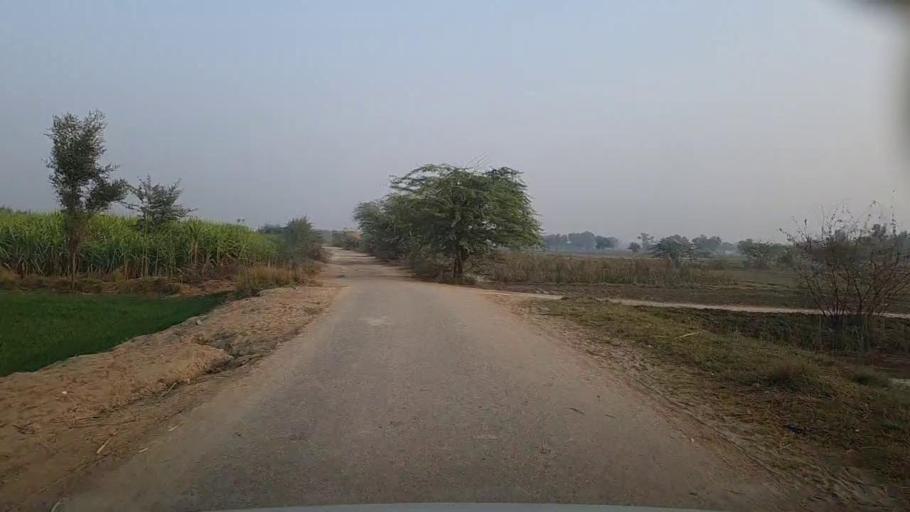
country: PK
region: Sindh
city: Bozdar
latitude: 27.0757
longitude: 68.5846
